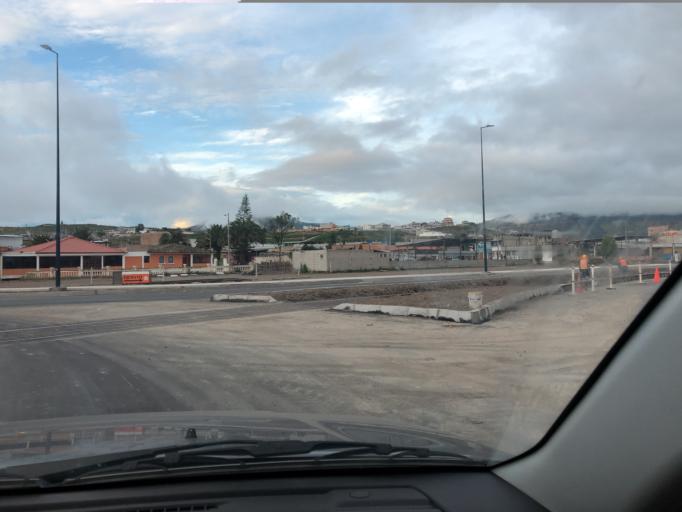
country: EC
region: Imbabura
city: Ibarra
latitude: 0.3561
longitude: -78.1392
